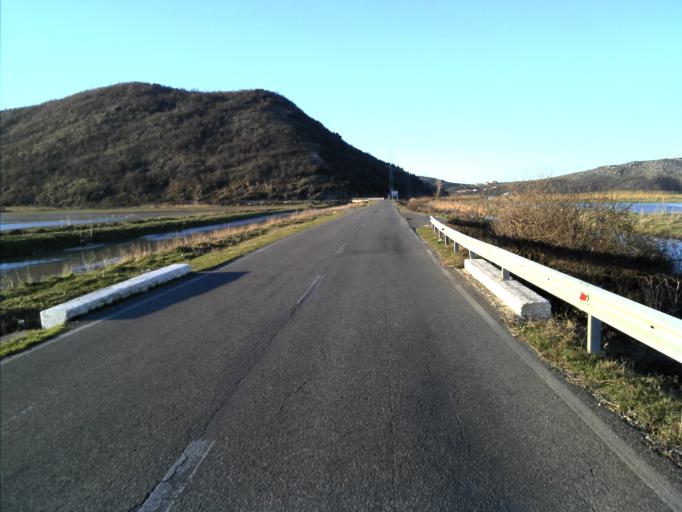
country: AL
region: Shkoder
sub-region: Rrethi i Shkodres
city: Dajc
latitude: 41.9335
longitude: 19.4426
